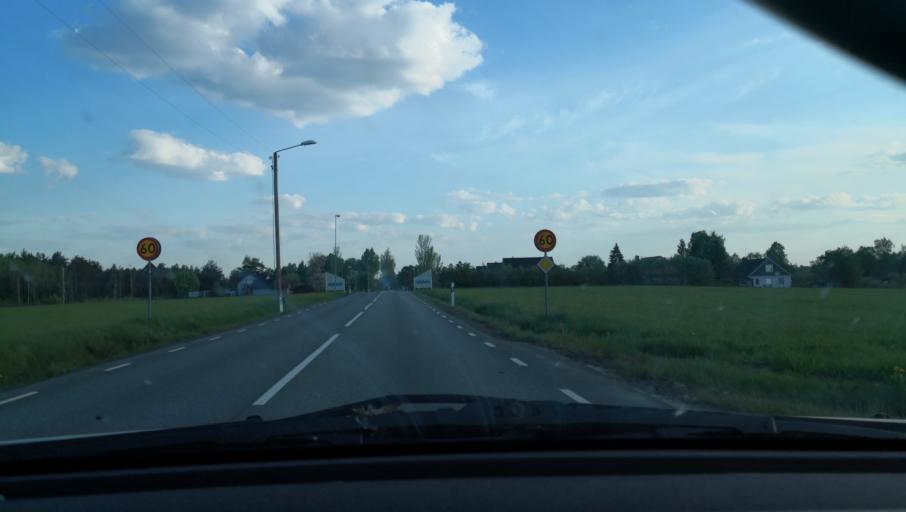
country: SE
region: Joenkoeping
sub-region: Nassjo Kommun
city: Bodafors
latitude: 57.5507
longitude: 14.7008
